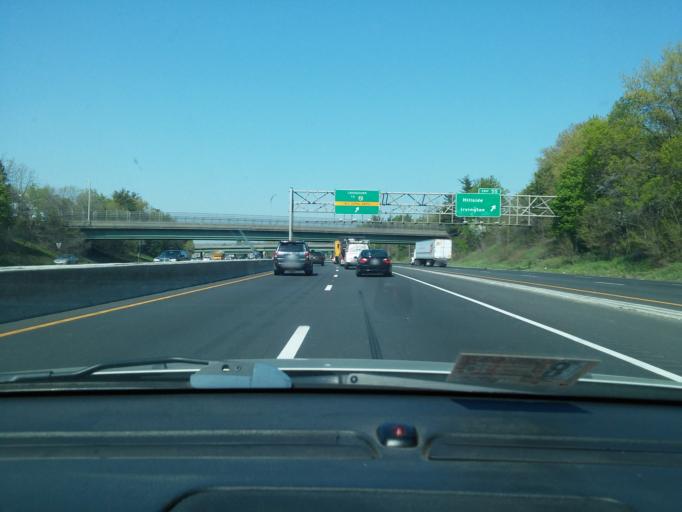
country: US
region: New Jersey
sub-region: Union County
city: Hillside
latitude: 40.7167
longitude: -74.2137
